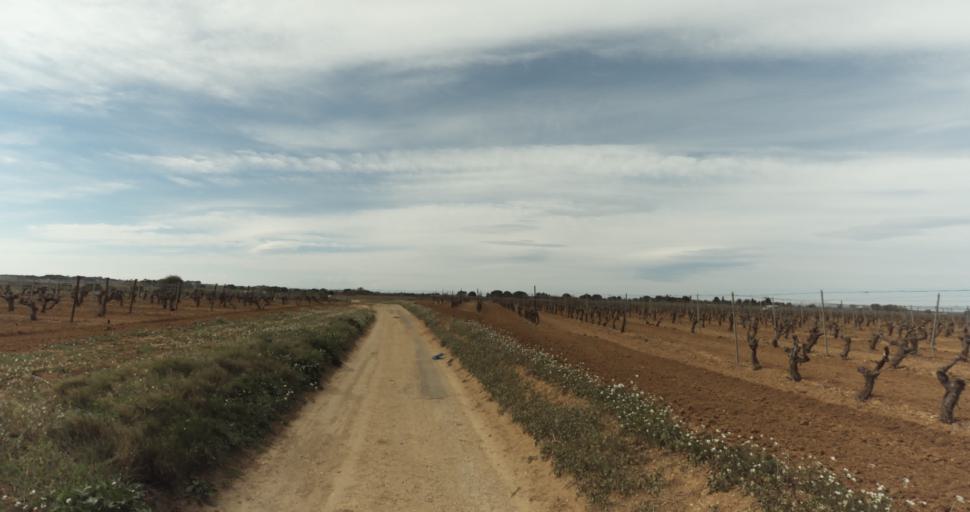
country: FR
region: Languedoc-Roussillon
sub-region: Departement de l'Herault
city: Marseillan
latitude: 43.3441
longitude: 3.5195
